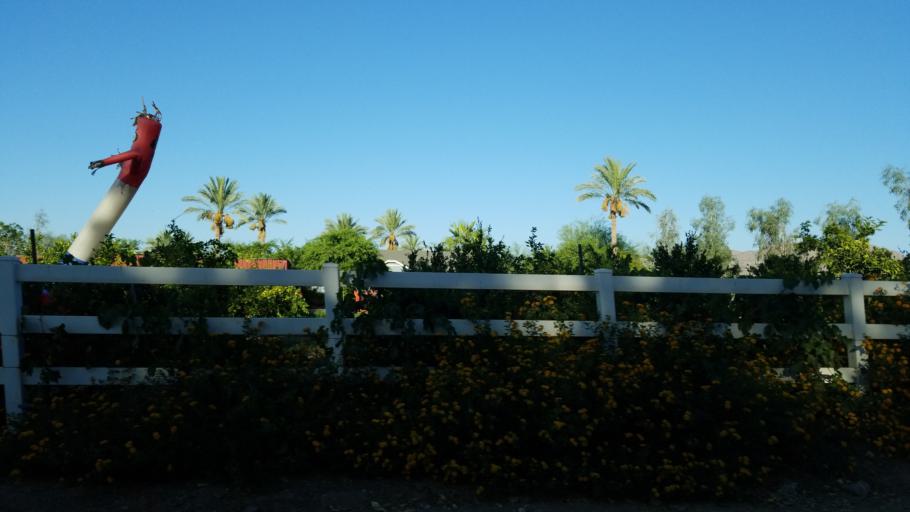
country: US
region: Arizona
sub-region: Maricopa County
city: Laveen
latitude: 33.3652
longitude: -112.1176
